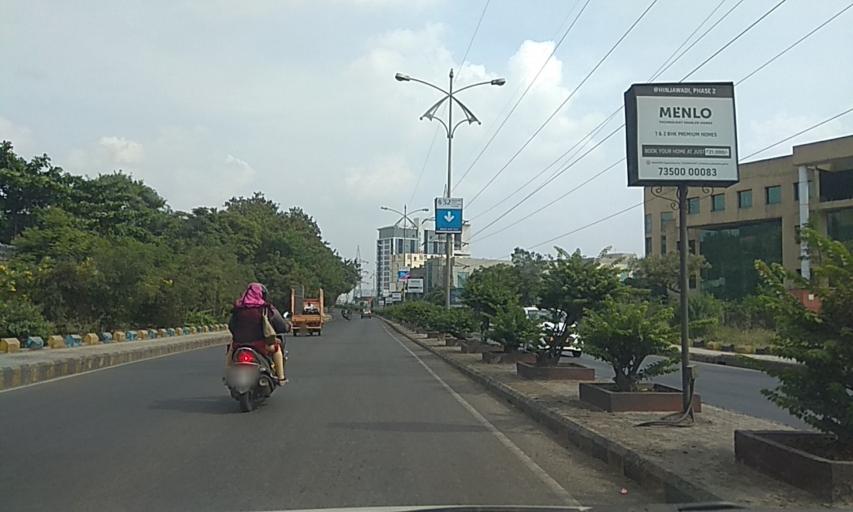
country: IN
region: Maharashtra
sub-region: Pune Division
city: Pimpri
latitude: 18.5962
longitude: 73.7140
